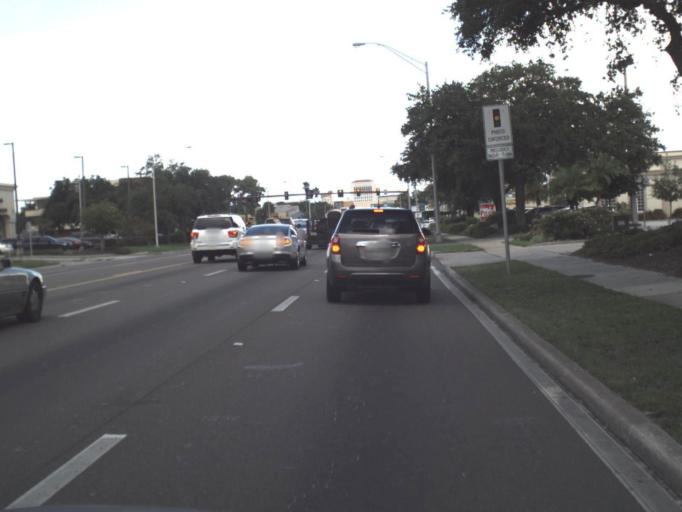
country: US
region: Florida
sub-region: Sarasota County
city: Sarasota
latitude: 27.3216
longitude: -82.5296
